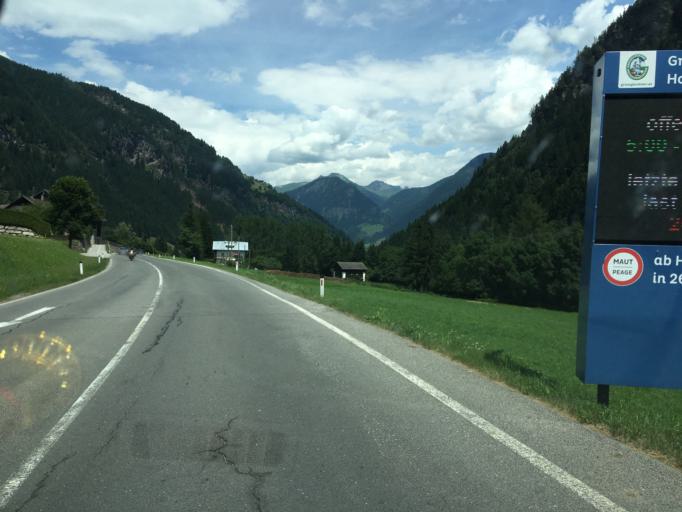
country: AT
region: Carinthia
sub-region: Politischer Bezirk Spittal an der Drau
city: Winklern
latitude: 46.8732
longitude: 12.8797
